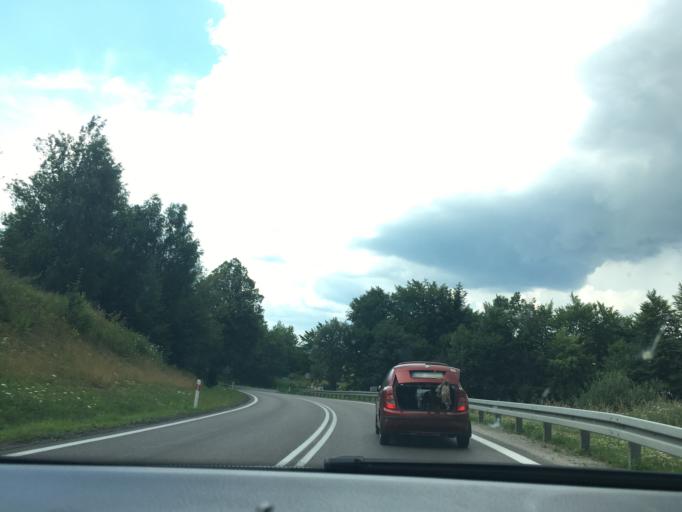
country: PL
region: Subcarpathian Voivodeship
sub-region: Powiat brzozowski
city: Jablonica Polska
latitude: 49.7297
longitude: 21.9073
